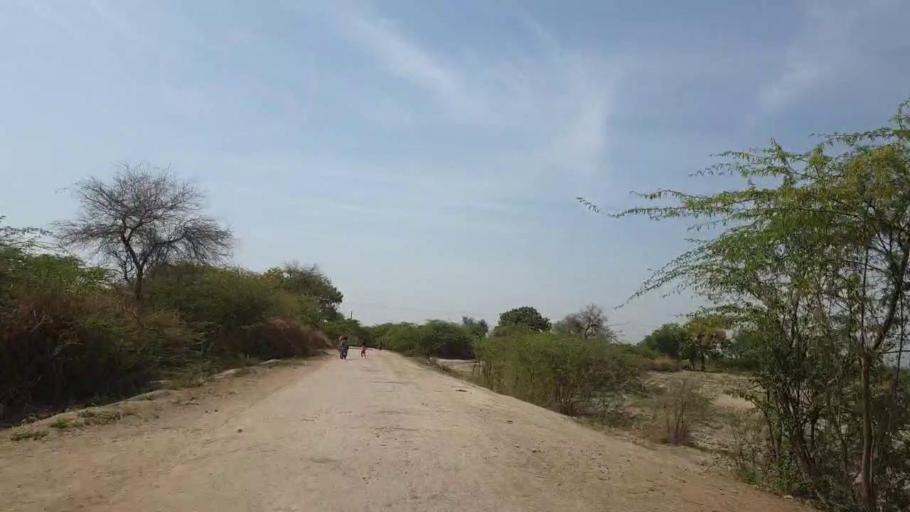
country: PK
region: Sindh
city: Kunri
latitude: 25.2051
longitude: 69.5420
